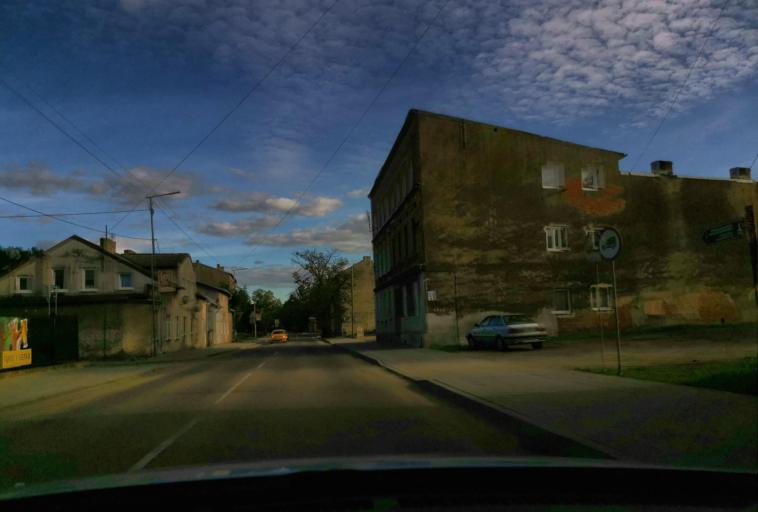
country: RU
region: Kaliningrad
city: Chernyakhovsk
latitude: 54.6271
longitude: 21.8131
